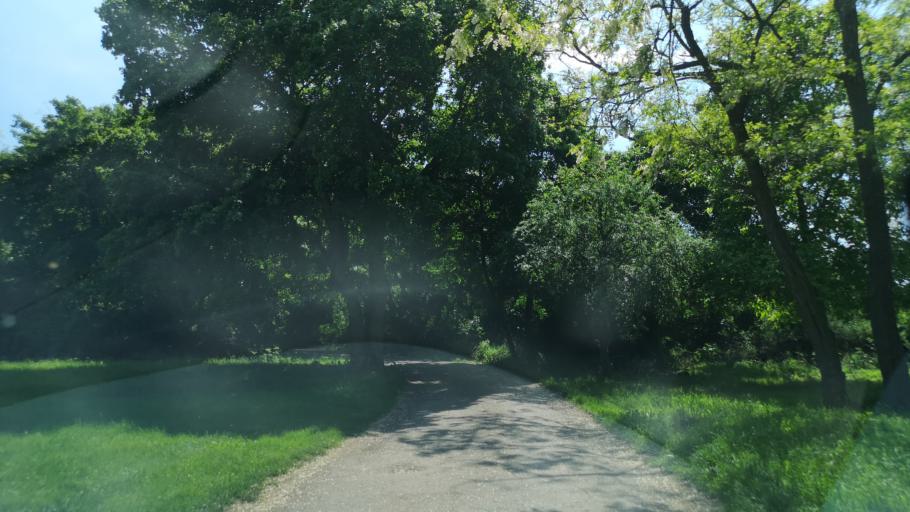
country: SK
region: Nitriansky
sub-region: Okres Nitra
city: Nitra
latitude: 48.2600
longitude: 18.0816
